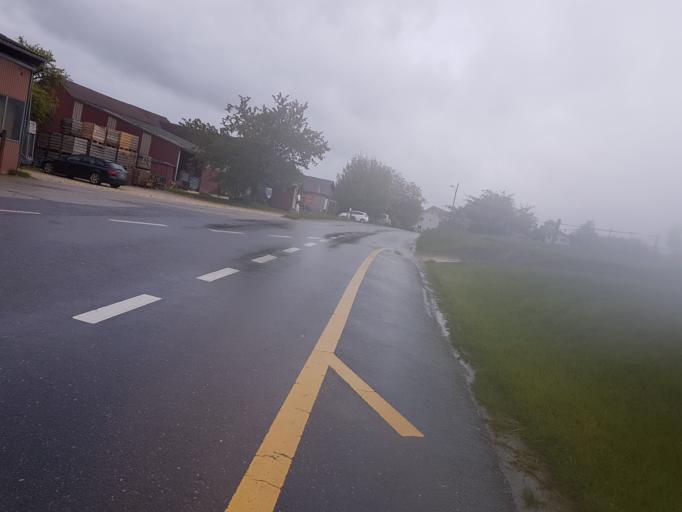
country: CH
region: Vaud
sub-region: Gros-de-Vaud District
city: Penthalaz
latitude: 46.6379
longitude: 6.5305
